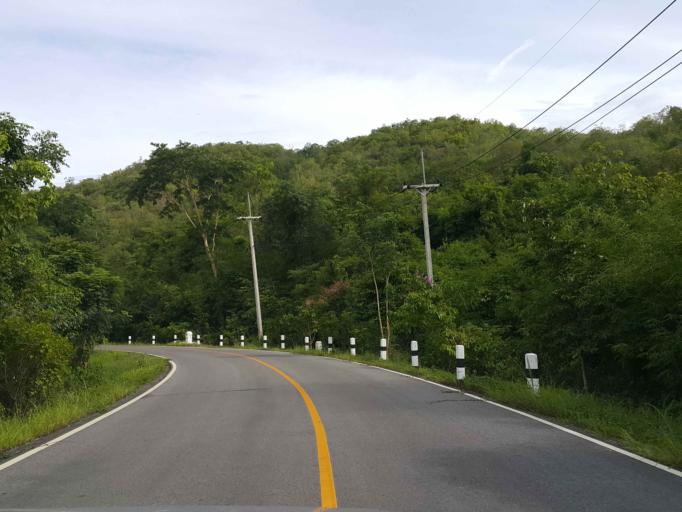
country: TH
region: Sukhothai
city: Thung Saliam
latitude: 17.2448
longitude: 99.4929
